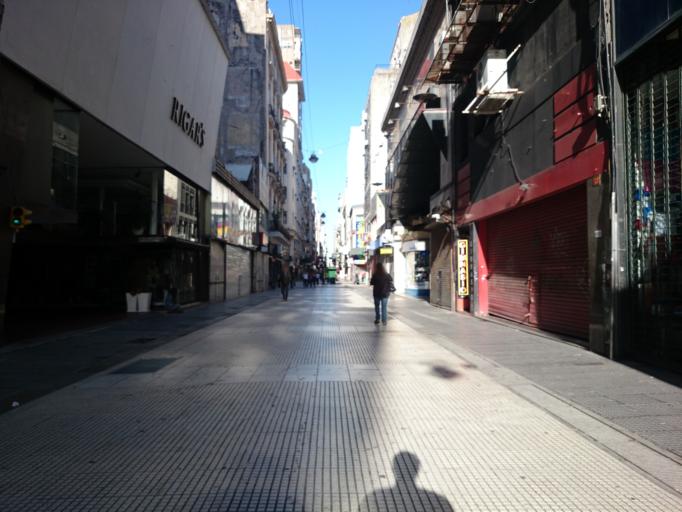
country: AR
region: Buenos Aires F.D.
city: Buenos Aires
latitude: -34.6023
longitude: -58.3759
